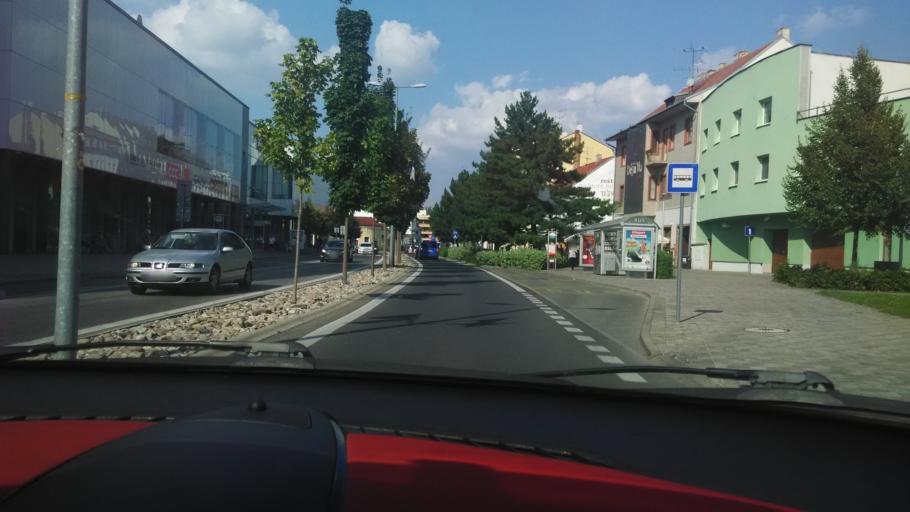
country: SK
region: Trnavsky
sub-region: Okres Trnava
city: Piestany
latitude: 48.5875
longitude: 17.8335
